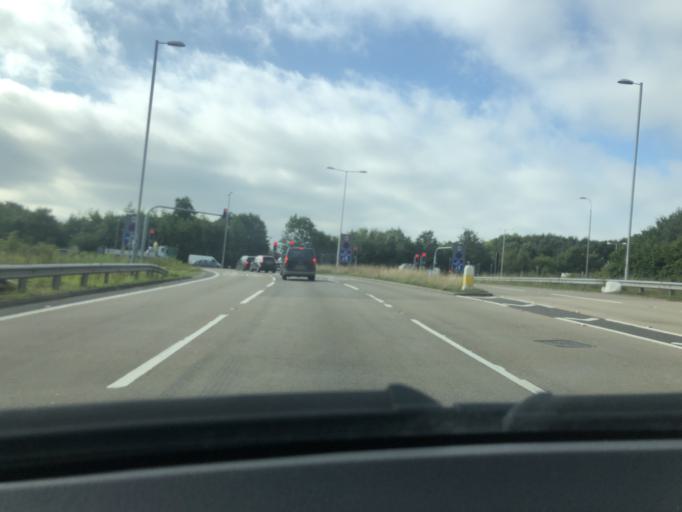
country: GB
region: England
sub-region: Devon
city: Heavitree
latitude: 50.7294
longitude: -3.4651
